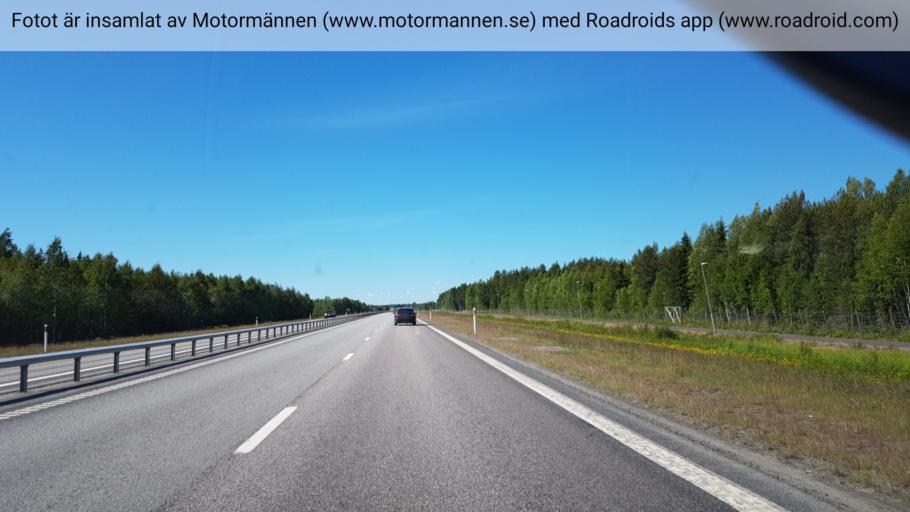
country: SE
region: Norrbotten
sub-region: Lulea Kommun
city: Sodra Sunderbyn
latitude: 65.5434
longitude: 21.8296
